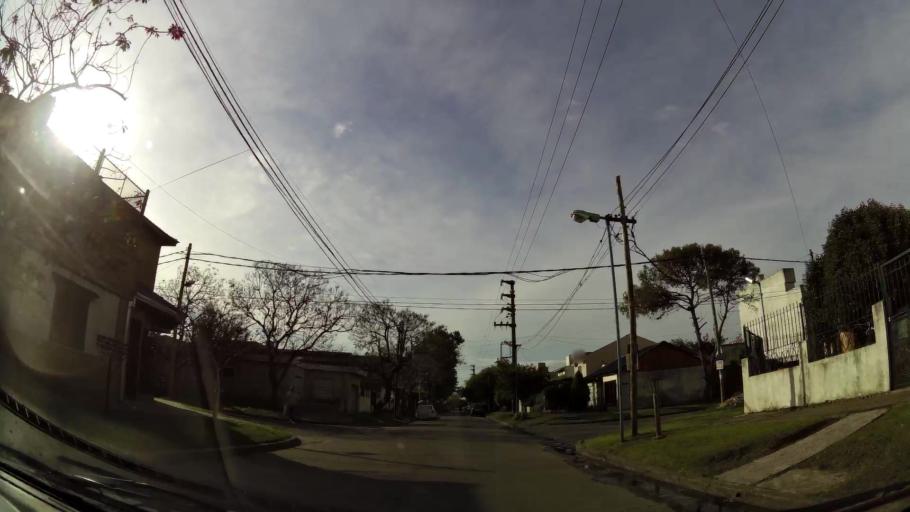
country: AR
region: Buenos Aires
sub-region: Partido de Quilmes
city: Quilmes
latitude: -34.7412
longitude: -58.2661
